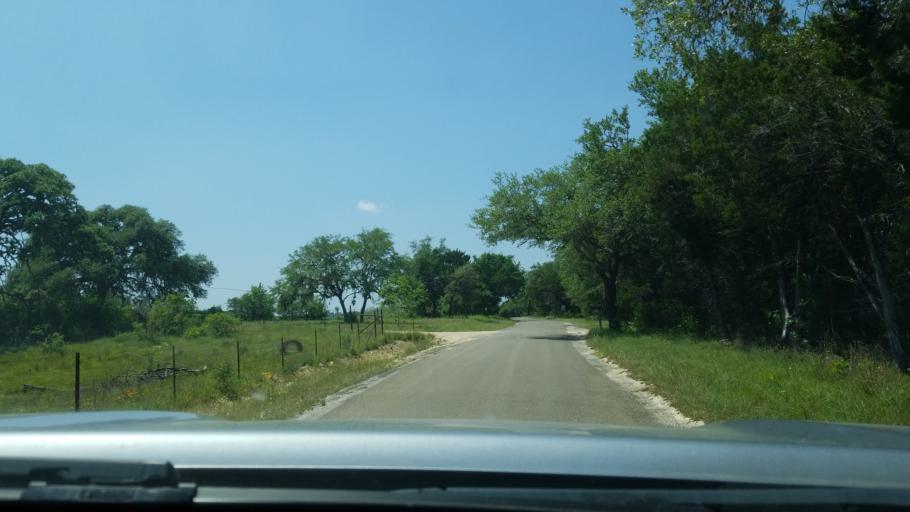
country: US
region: Texas
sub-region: Blanco County
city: Blanco
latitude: 30.0030
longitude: -98.4253
